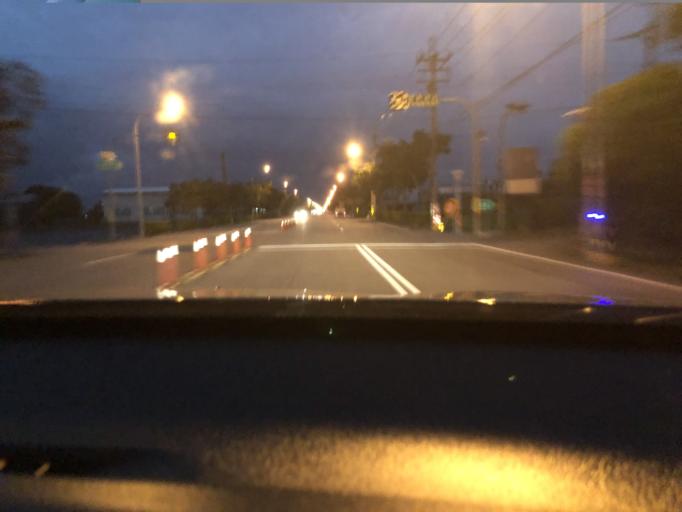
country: TW
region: Taiwan
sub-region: Hualien
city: Hualian
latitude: 23.9487
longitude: 121.5658
